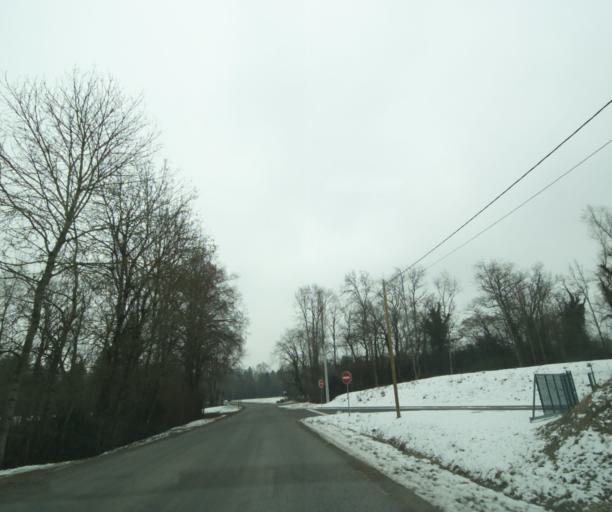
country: FR
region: Rhone-Alpes
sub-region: Departement de la Haute-Savoie
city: Pers-Jussy
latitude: 46.1204
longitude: 6.2899
